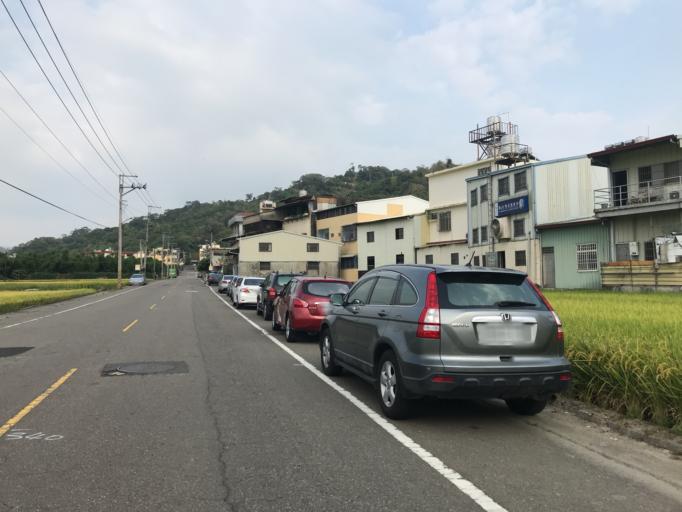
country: TW
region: Taiwan
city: Zhongxing New Village
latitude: 24.0405
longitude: 120.6955
